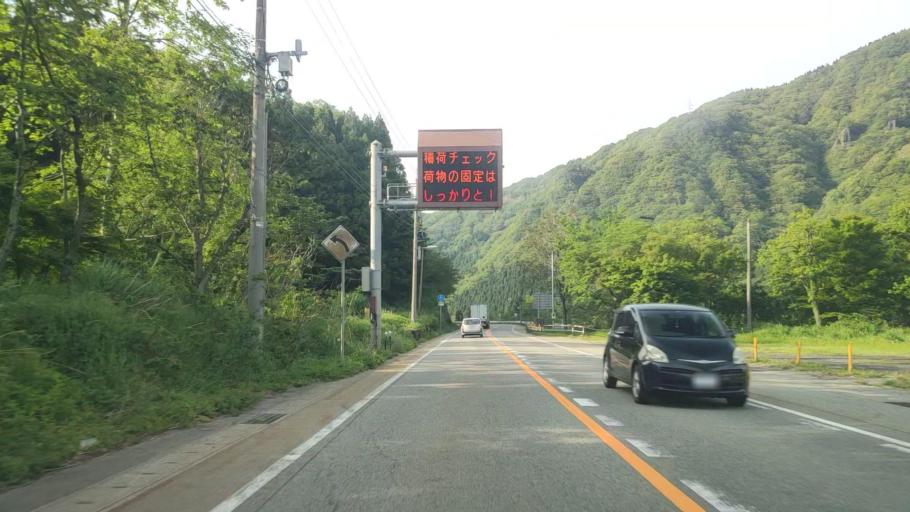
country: JP
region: Toyama
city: Yatsuomachi-higashikumisaka
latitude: 36.5405
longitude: 137.2293
